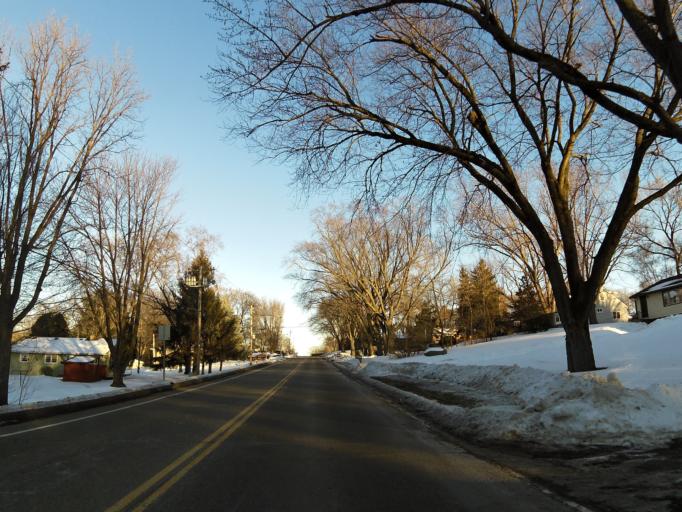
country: US
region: Minnesota
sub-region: Ramsey County
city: North Saint Paul
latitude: 45.0208
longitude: -93.0285
